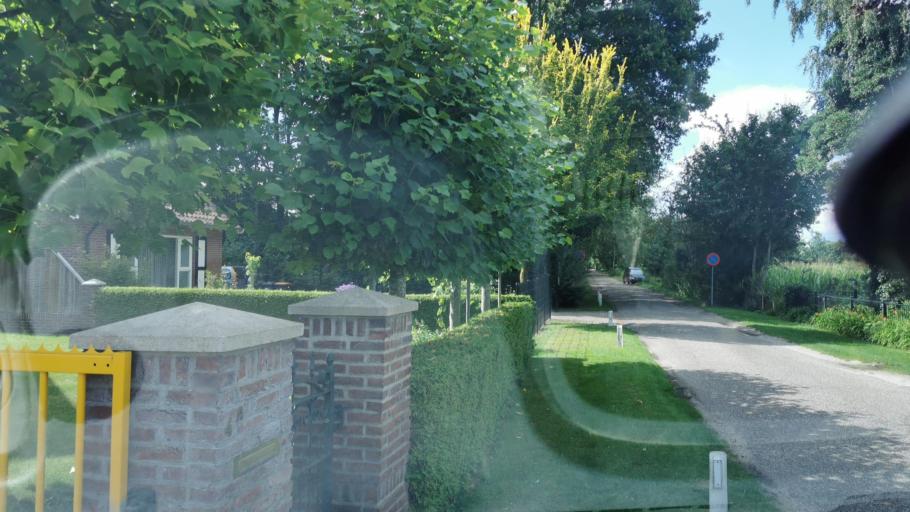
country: DE
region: North Rhine-Westphalia
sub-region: Regierungsbezirk Munster
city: Gronau
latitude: 52.2405
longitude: 7.0408
